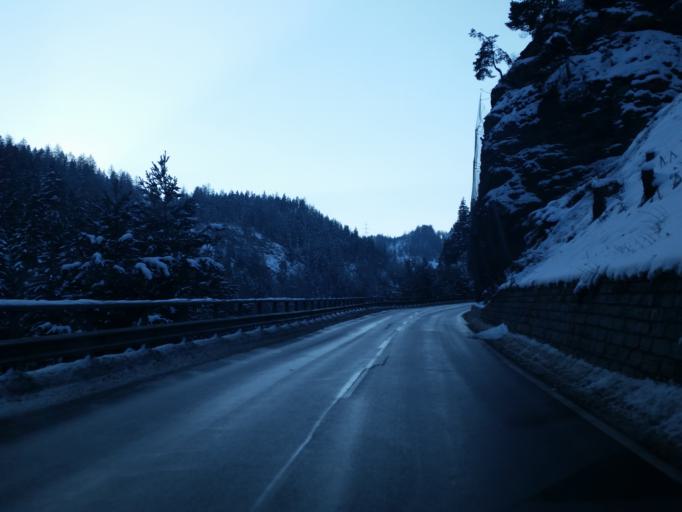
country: CH
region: Grisons
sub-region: Inn District
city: Scuol
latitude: 46.7768
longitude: 10.2365
